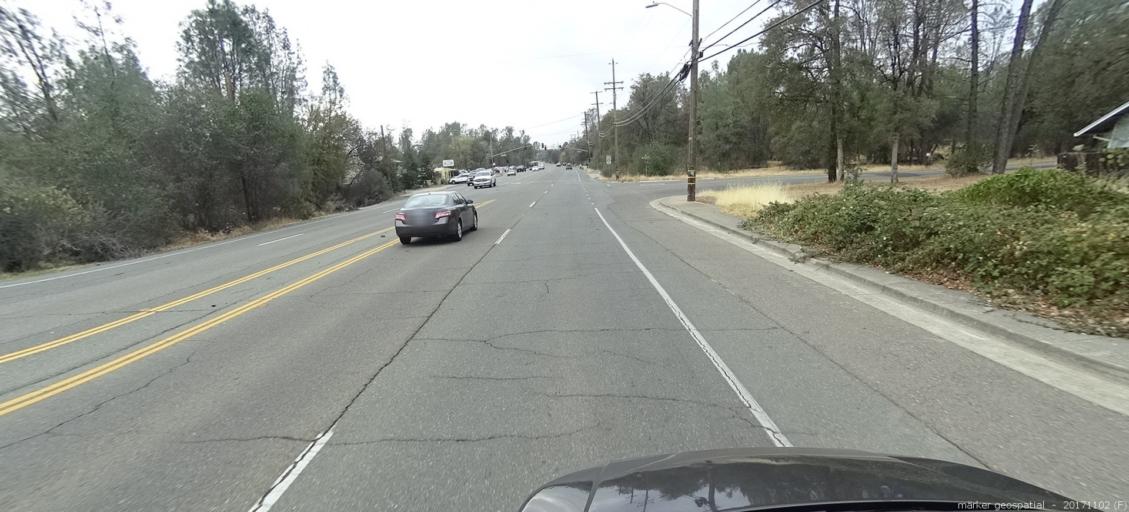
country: US
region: California
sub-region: Shasta County
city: Redding
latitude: 40.6325
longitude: -122.4050
